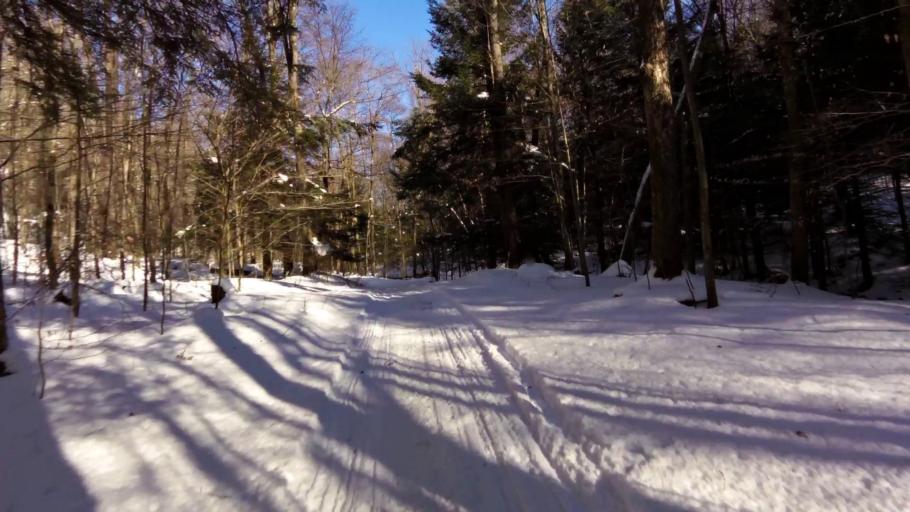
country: US
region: Pennsylvania
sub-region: McKean County
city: Bradford
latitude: 42.0108
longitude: -78.7956
